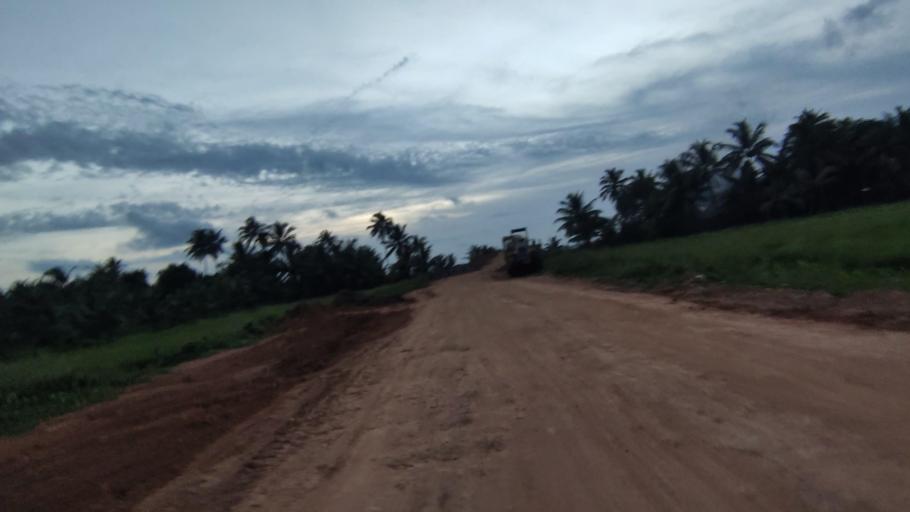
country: IN
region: Kerala
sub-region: Kottayam
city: Kottayam
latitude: 9.6438
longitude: 76.4524
